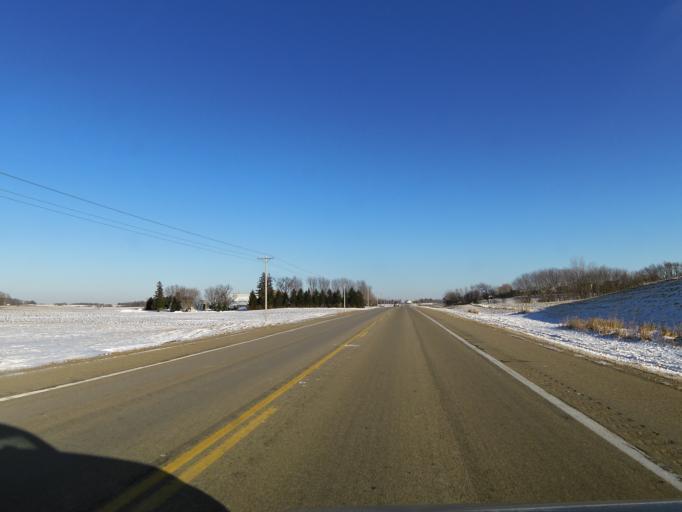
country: US
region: Minnesota
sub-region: Rice County
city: Lonsdale
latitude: 44.4863
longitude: -93.4507
